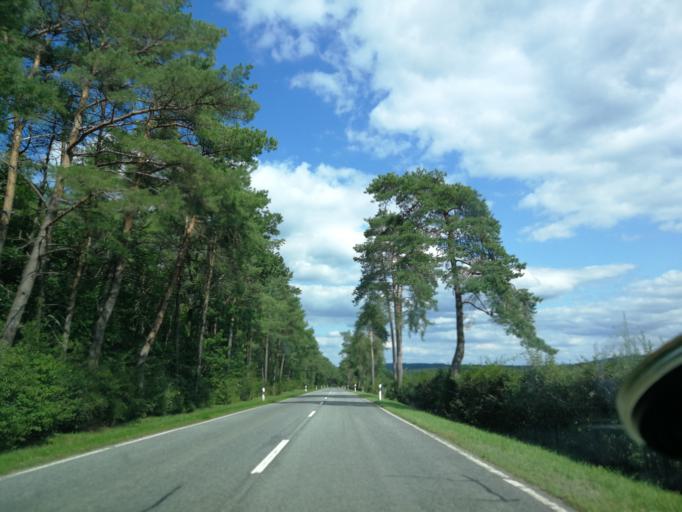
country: DE
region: Rheinland-Pfalz
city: Oberehe-Stroheich
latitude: 50.3018
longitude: 6.7620
